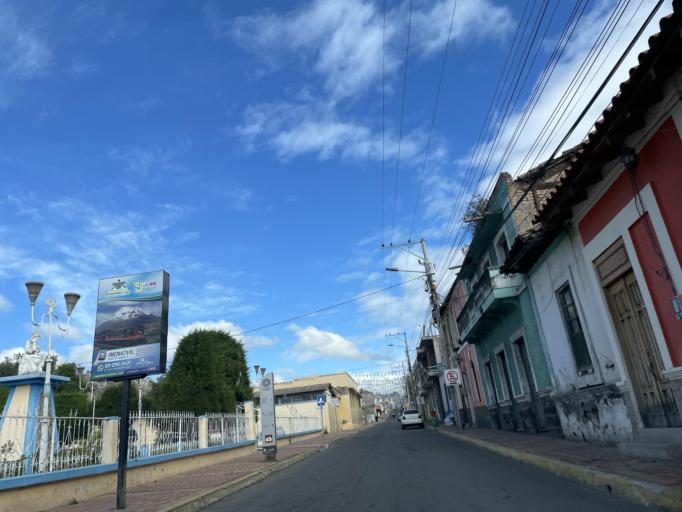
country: EC
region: Chimborazo
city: Guano
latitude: -1.6078
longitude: -78.6342
